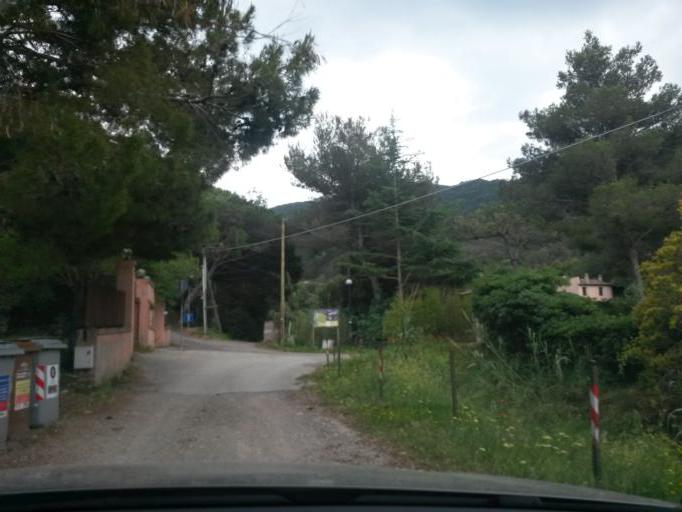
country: IT
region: Tuscany
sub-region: Provincia di Livorno
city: Rio nell'Elba
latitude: 42.8323
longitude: 10.3875
